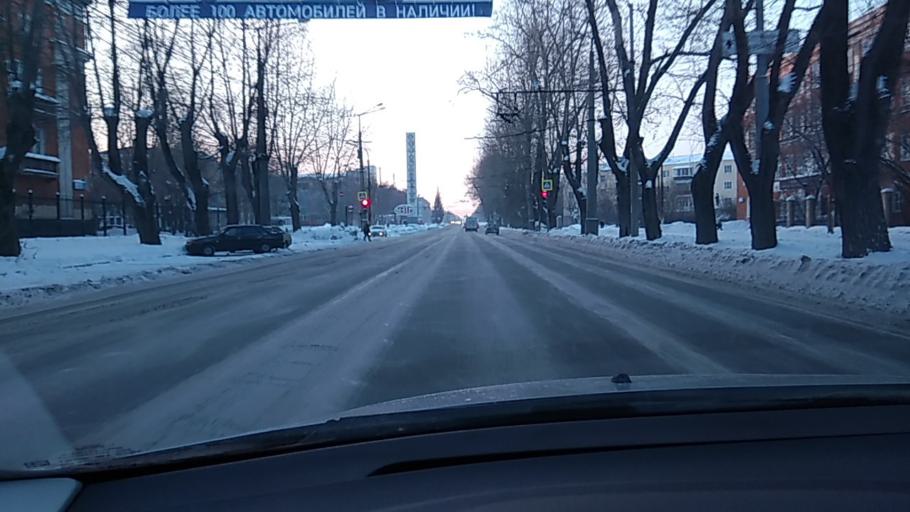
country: RU
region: Sverdlovsk
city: Yekaterinburg
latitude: 56.8865
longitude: 60.5993
